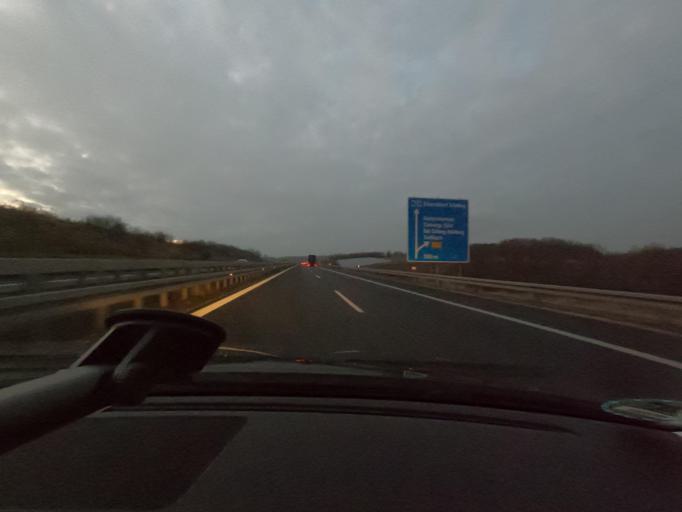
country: DE
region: Bavaria
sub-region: Upper Franconia
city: Lichtenfels
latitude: 50.1560
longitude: 11.0202
